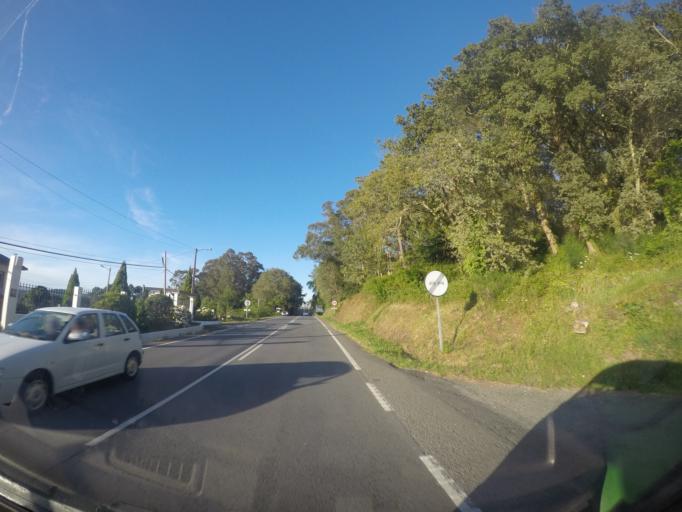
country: ES
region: Galicia
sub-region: Provincia da Coruna
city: Noia
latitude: 42.7824
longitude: -8.9254
